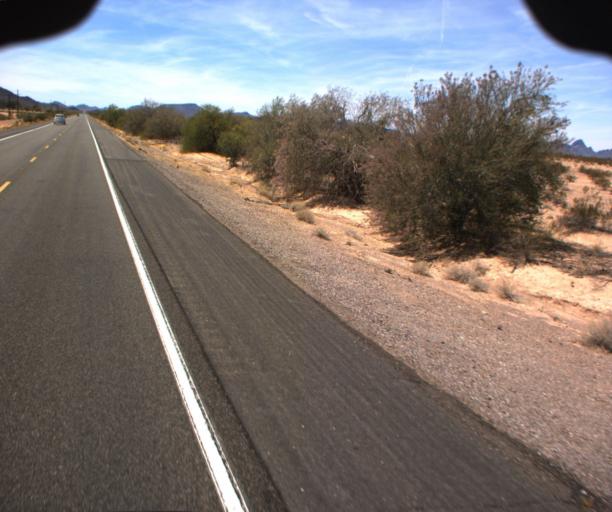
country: US
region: Arizona
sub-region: La Paz County
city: Salome
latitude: 33.6959
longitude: -113.8765
